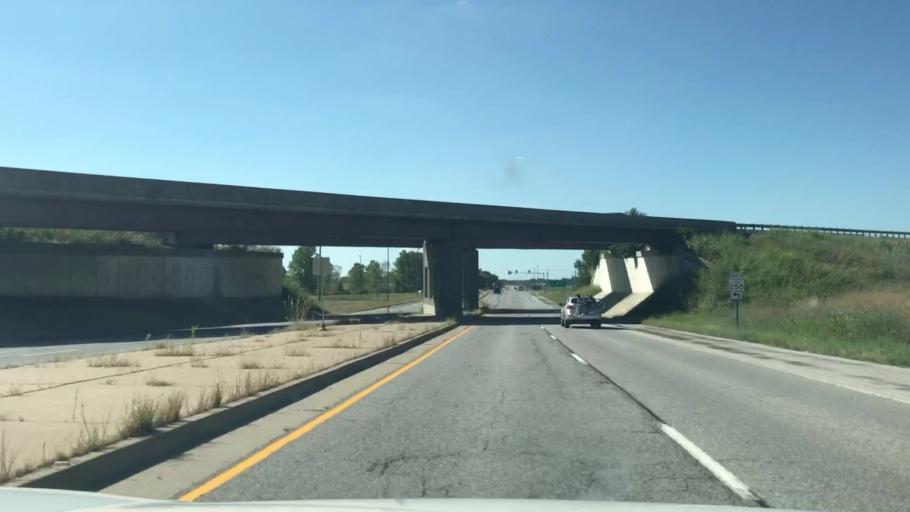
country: US
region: Illinois
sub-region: Madison County
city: South Roxana
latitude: 38.8501
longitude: -90.0509
